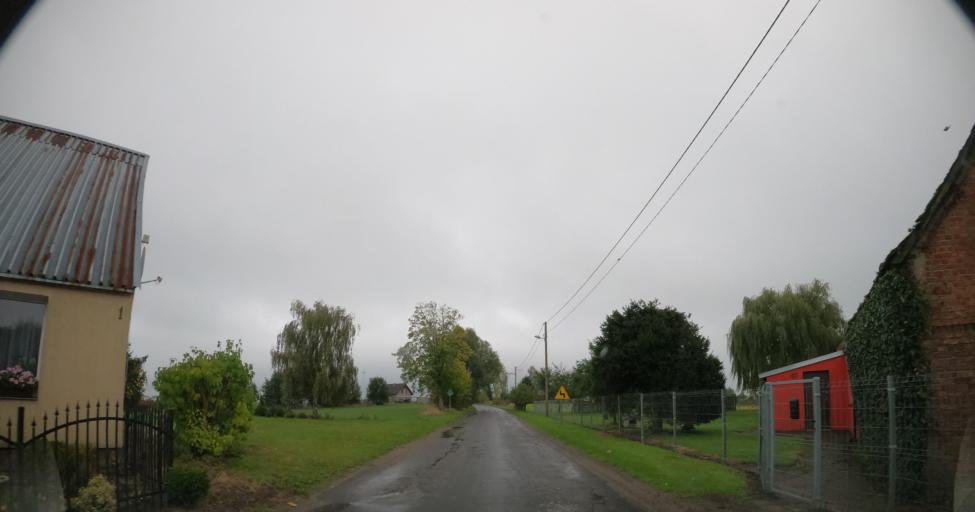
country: PL
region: West Pomeranian Voivodeship
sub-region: Powiat pyrzycki
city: Kozielice
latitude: 53.0906
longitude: 14.7714
